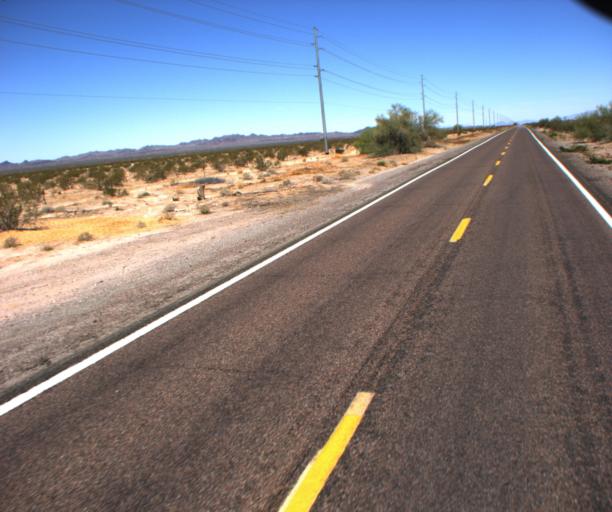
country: US
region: Arizona
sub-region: La Paz County
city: Salome
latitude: 33.8814
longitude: -113.9465
